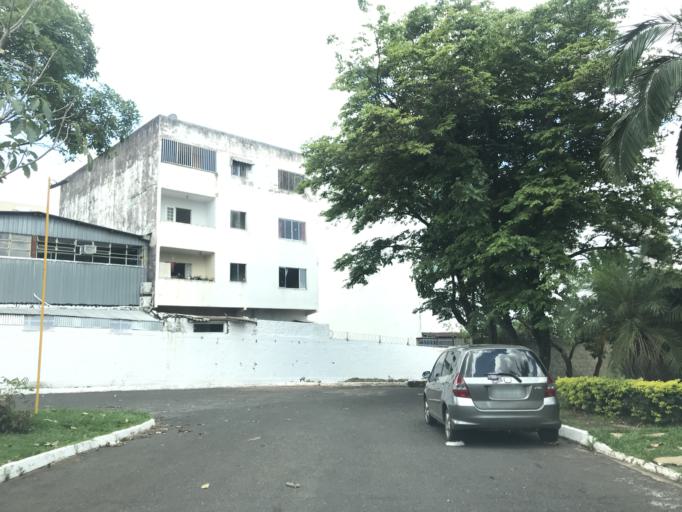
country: BR
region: Federal District
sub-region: Brasilia
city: Brasilia
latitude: -15.6816
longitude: -47.8330
